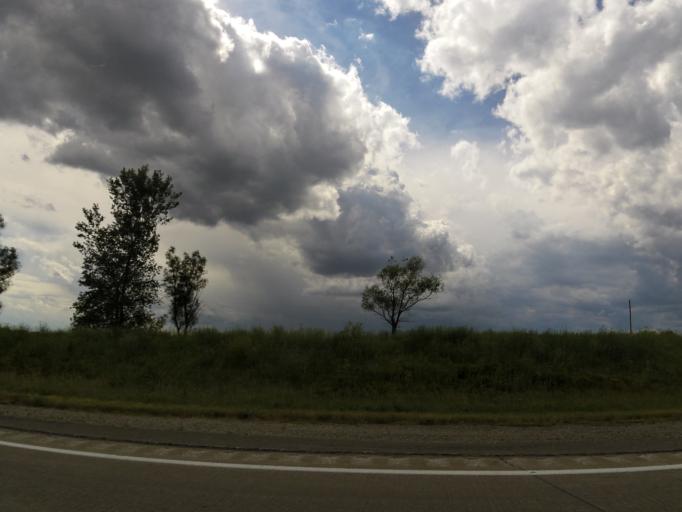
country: US
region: Iowa
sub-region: Washington County
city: Washington
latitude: 41.2746
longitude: -91.5374
